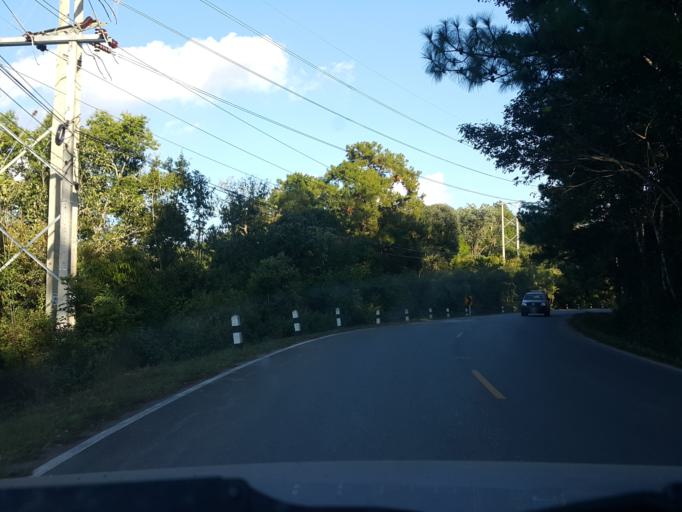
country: TH
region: Mae Hong Son
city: Mae Hi
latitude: 19.2721
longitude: 98.5629
